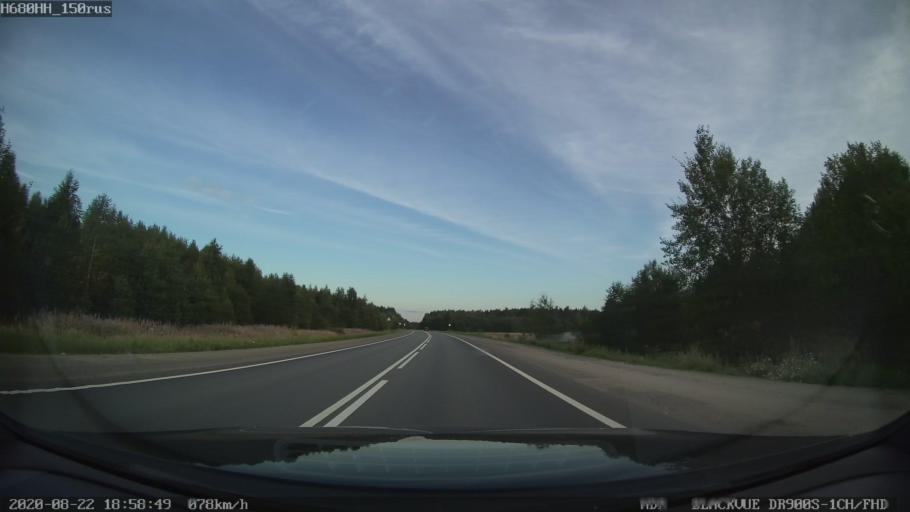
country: RU
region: Tverskaya
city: Rameshki
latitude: 57.1499
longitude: 36.0814
